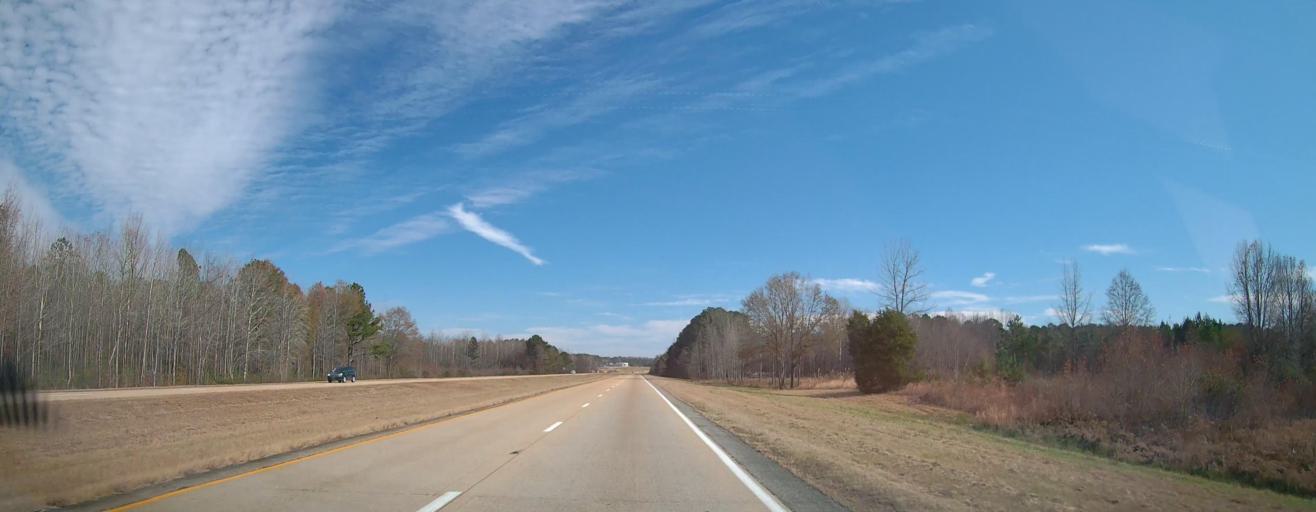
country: US
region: Mississippi
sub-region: Tishomingo County
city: Iuka
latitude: 34.8048
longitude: -88.2477
